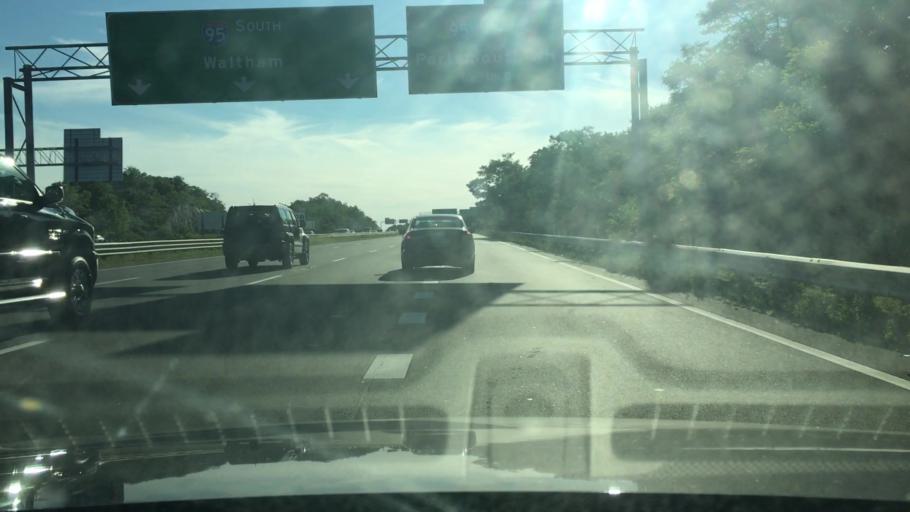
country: US
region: Massachusetts
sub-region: Essex County
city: South Peabody
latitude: 42.5259
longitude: -70.9641
